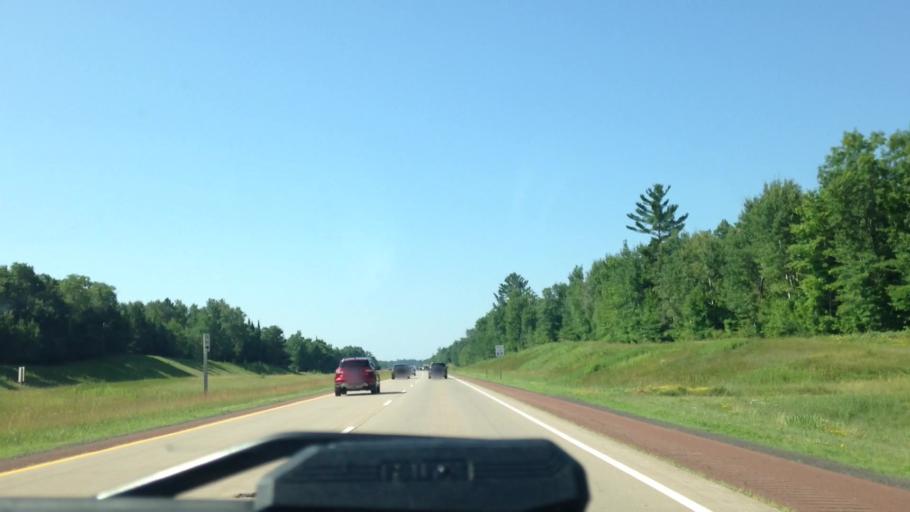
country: US
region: Wisconsin
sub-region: Douglas County
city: Lake Nebagamon
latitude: 46.3801
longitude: -91.8237
